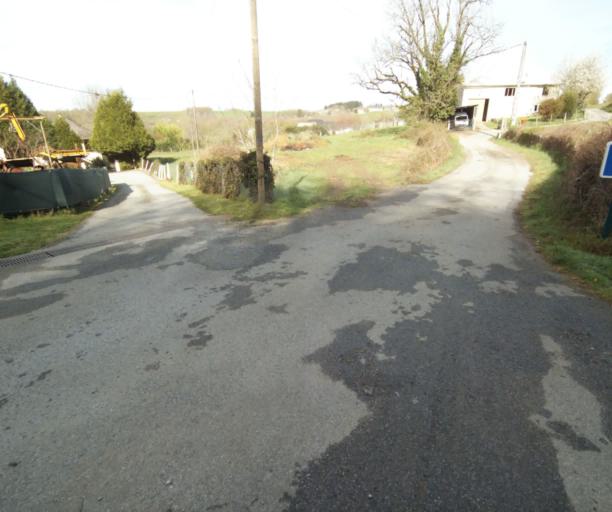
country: FR
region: Limousin
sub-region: Departement de la Correze
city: Laguenne
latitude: 45.2664
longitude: 1.8233
